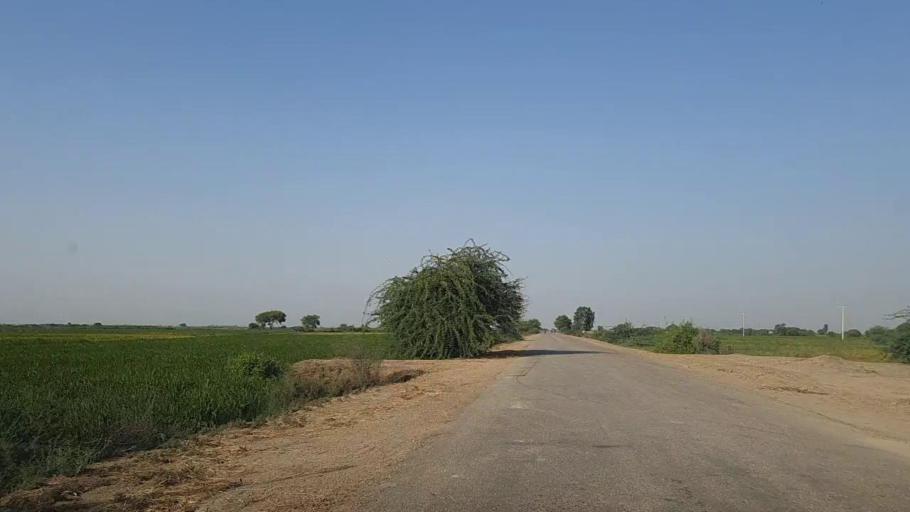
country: PK
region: Sindh
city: Mirpur Batoro
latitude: 24.5847
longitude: 68.3968
